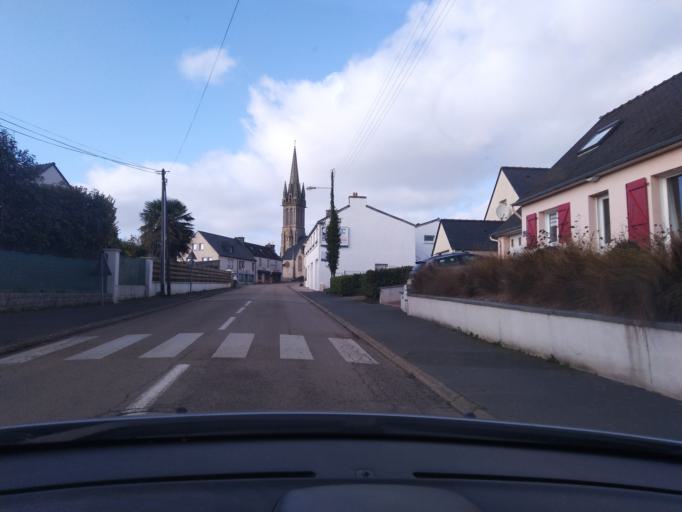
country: FR
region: Brittany
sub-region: Departement du Finistere
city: Plouigneau
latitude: 48.5658
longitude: -3.6999
